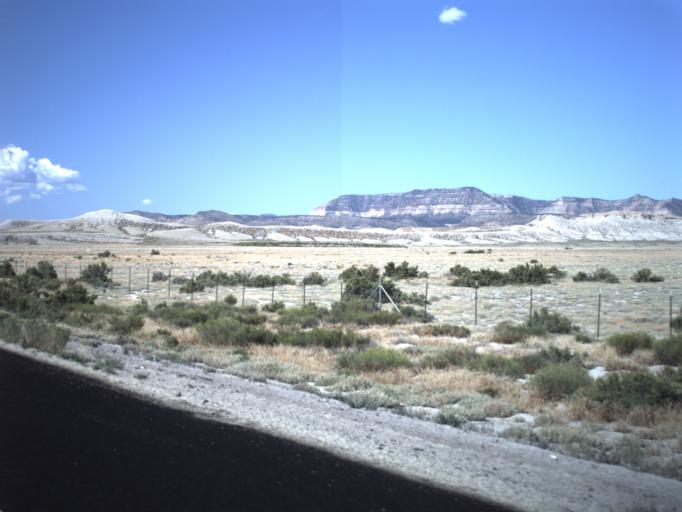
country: US
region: Utah
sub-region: Emery County
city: Ferron
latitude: 38.9944
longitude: -111.1661
